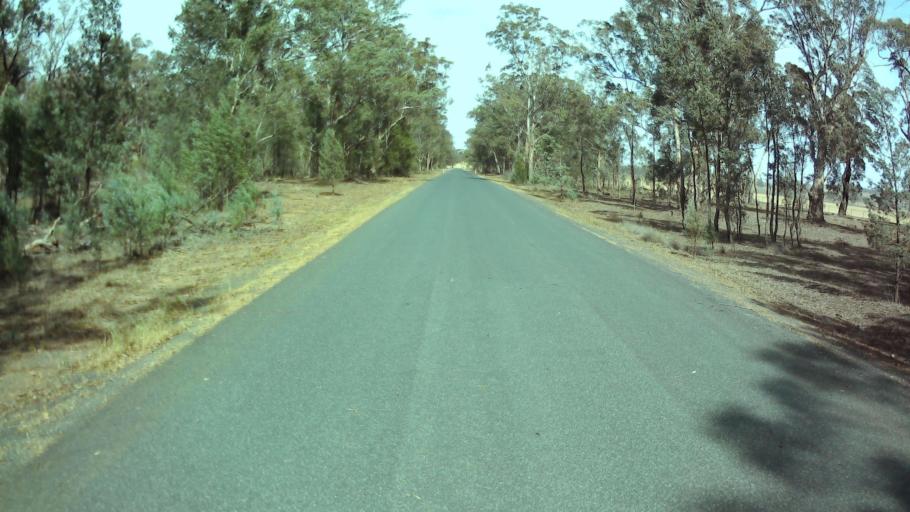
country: AU
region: New South Wales
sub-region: Weddin
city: Grenfell
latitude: -33.8086
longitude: 148.0741
